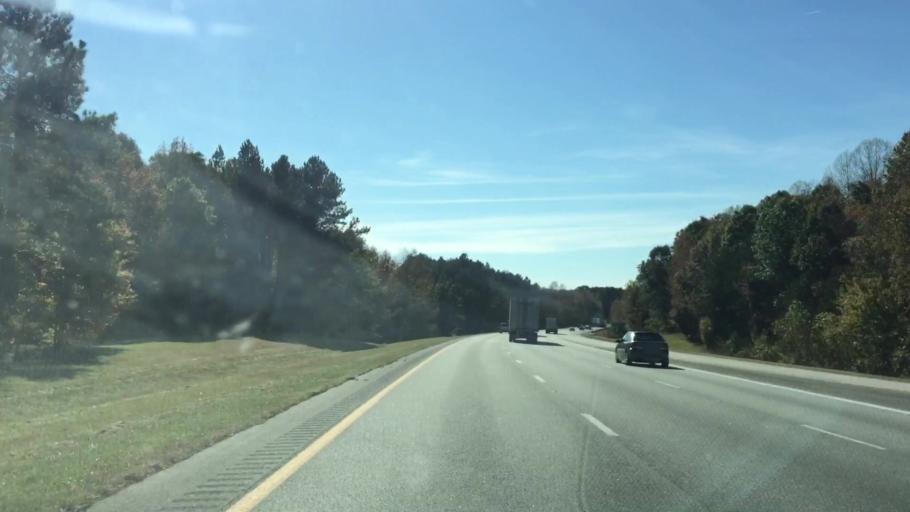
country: US
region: North Carolina
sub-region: Davidson County
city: Lexington
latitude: 35.8072
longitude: -80.1851
